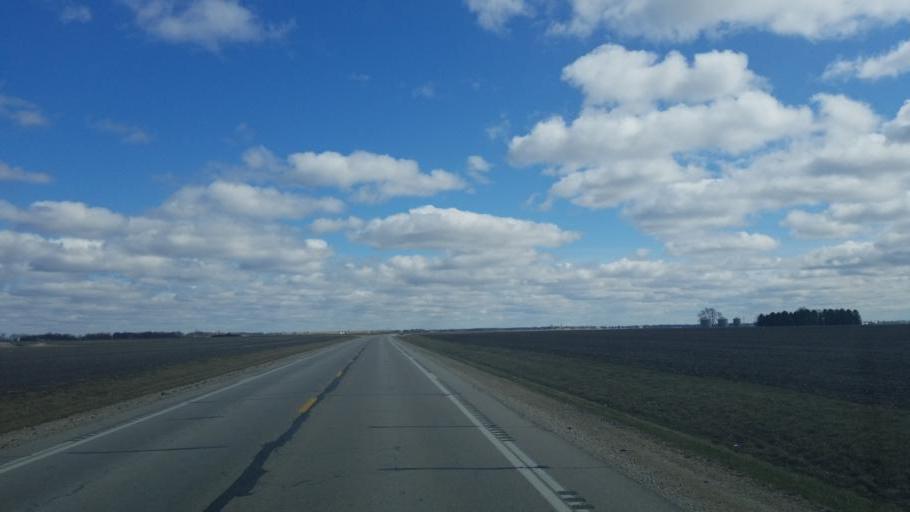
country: US
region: Illinois
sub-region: Douglas County
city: Villa Grove
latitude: 39.7919
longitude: -88.1081
